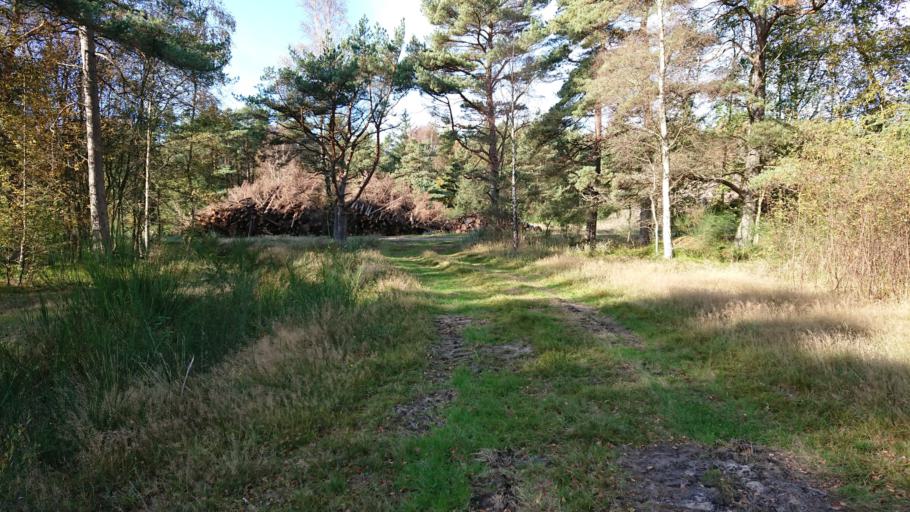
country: DK
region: North Denmark
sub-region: Frederikshavn Kommune
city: Strandby
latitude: 57.6388
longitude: 10.4478
